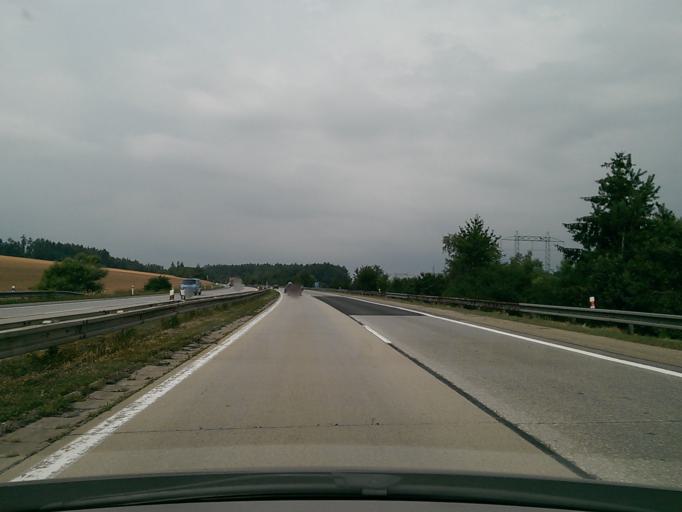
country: CZ
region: South Moravian
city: Ricany
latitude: 49.2547
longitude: 16.3469
